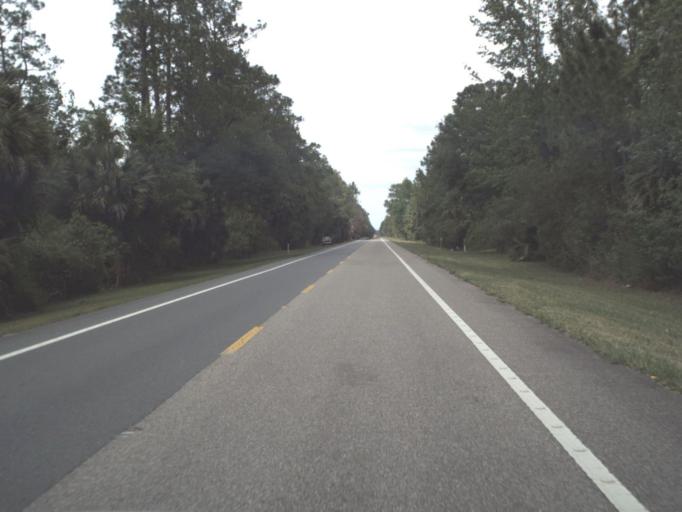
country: US
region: Florida
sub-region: Flagler County
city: Bunnell
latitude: 29.3752
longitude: -81.3111
